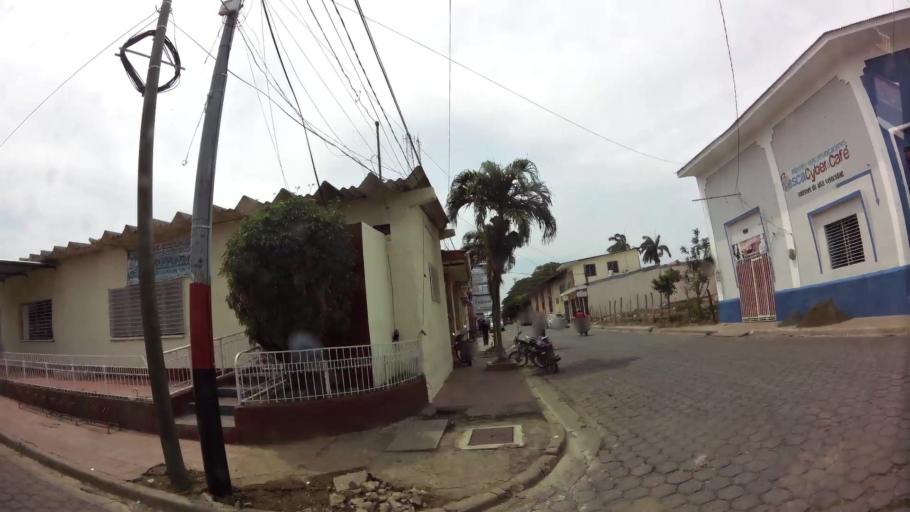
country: NI
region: Rivas
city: Rivas
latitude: 11.4376
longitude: -85.8288
